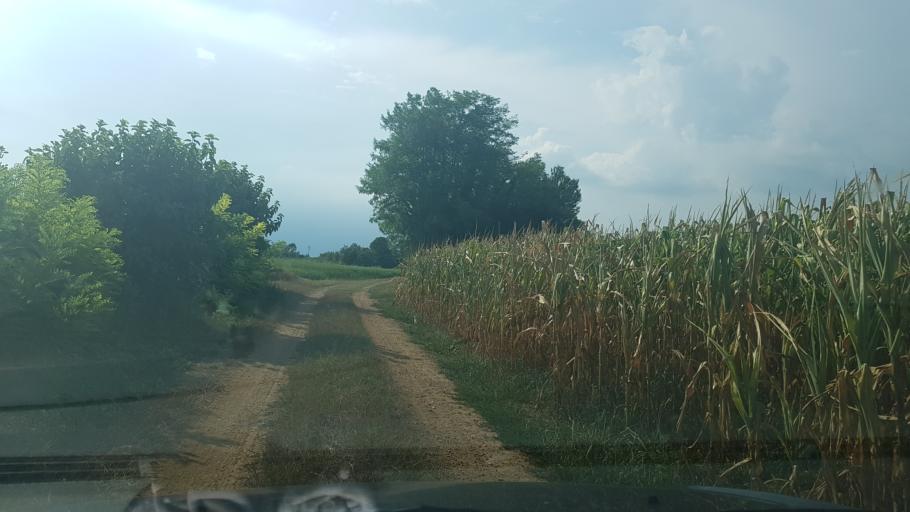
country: IT
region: Friuli Venezia Giulia
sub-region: Provincia di Udine
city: San Vito di Fagagna
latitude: 46.0605
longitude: 13.0830
